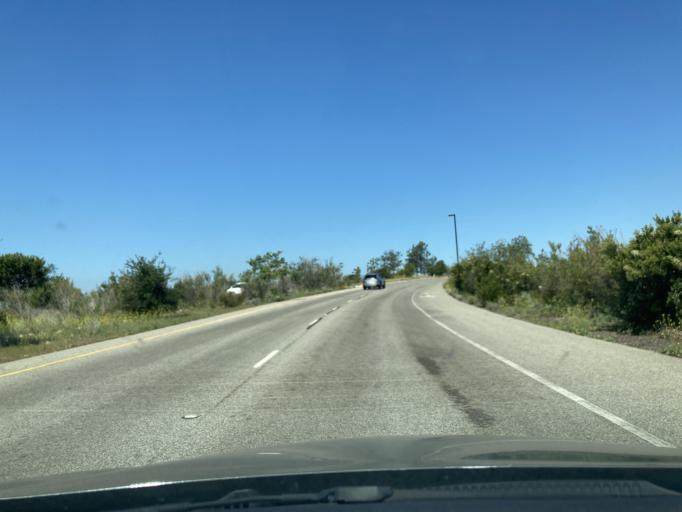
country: US
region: California
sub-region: Ventura County
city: Camarillo
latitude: 34.1700
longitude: -119.0523
